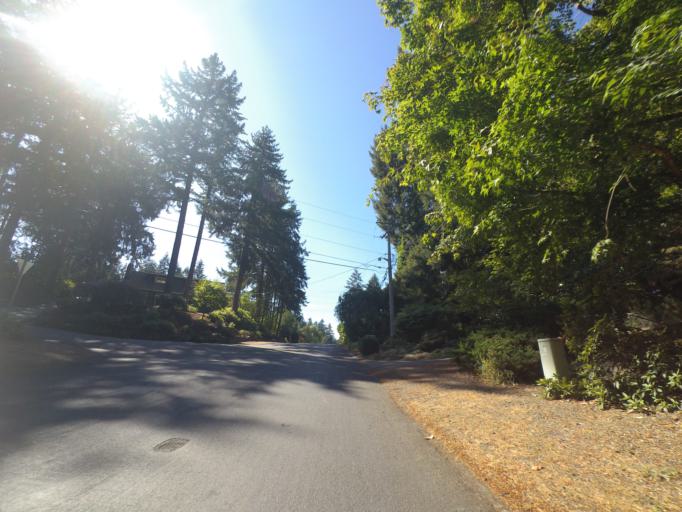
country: US
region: Washington
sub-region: Pierce County
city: Fircrest
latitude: 47.2142
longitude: -122.5252
